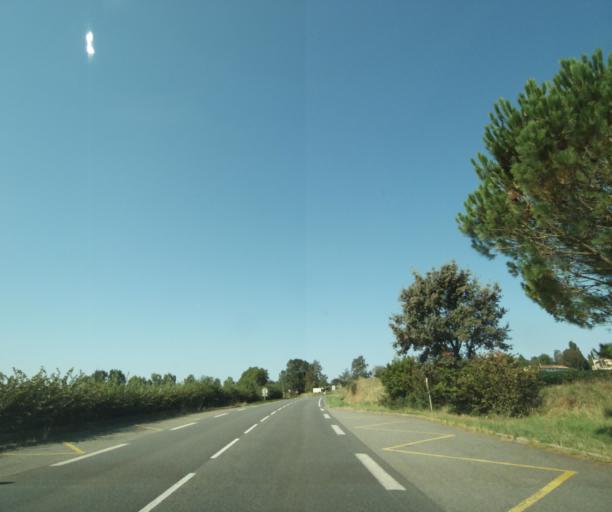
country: FR
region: Midi-Pyrenees
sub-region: Departement de la Haute-Garonne
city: Beaumont-sur-Leze
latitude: 43.3825
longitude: 1.3458
